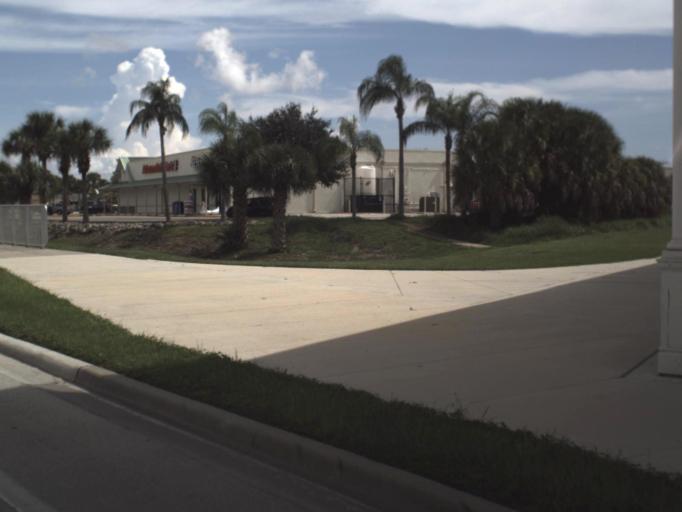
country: US
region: Florida
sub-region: Sarasota County
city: Nokomis
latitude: 27.1083
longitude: -82.4421
